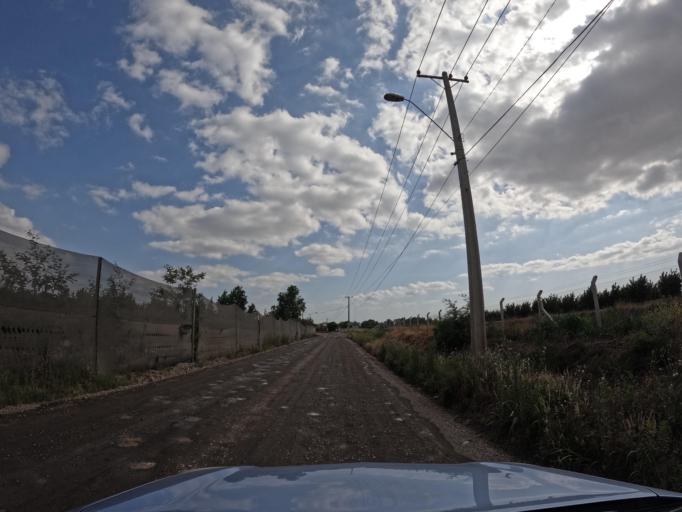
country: CL
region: Maule
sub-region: Provincia de Curico
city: Molina
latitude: -35.1680
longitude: -71.2912
